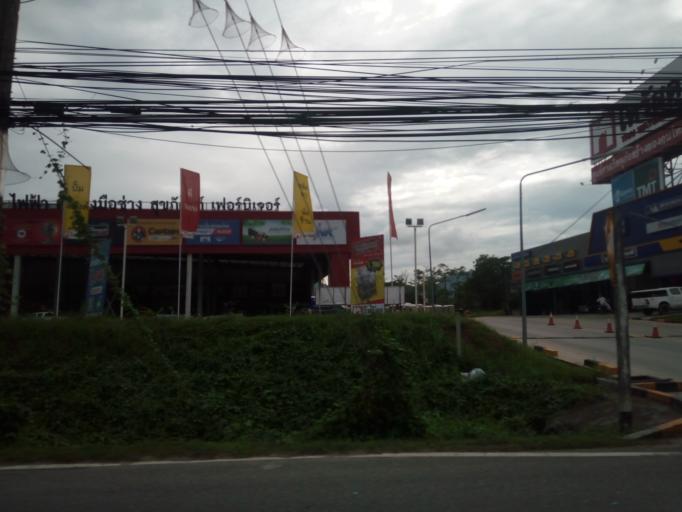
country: TH
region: Phuket
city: Thalang
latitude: 7.9863
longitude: 98.3583
